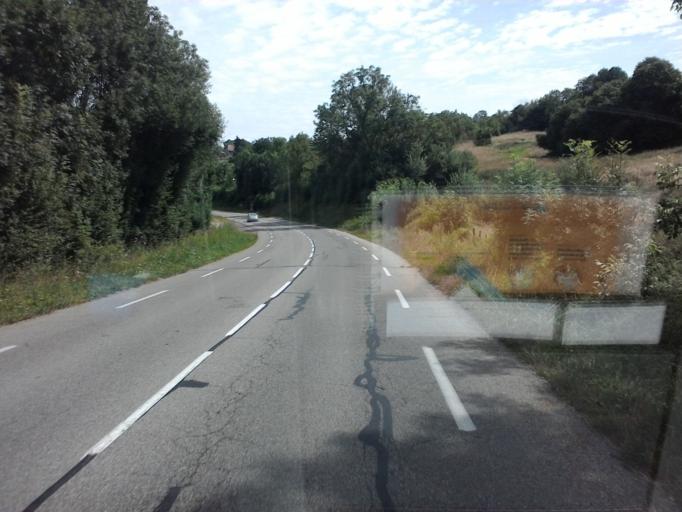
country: FR
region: Rhone-Alpes
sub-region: Departement de l'Isere
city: Bilieu
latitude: 45.4548
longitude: 5.5431
